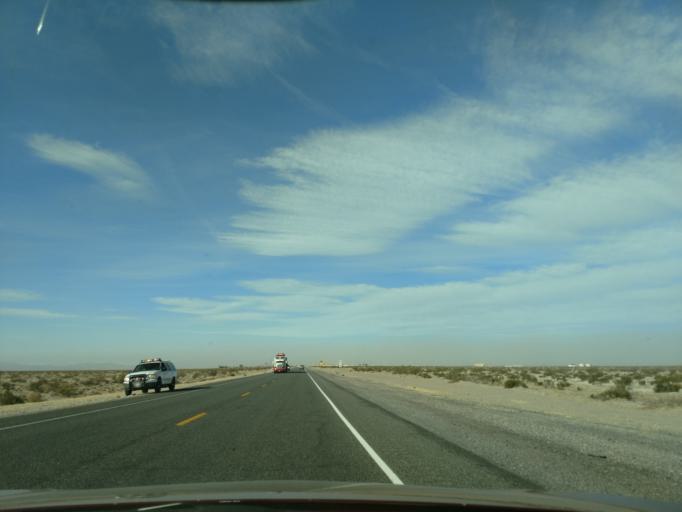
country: US
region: Nevada
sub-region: Nye County
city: Beatty
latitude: 36.6378
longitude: -116.3761
